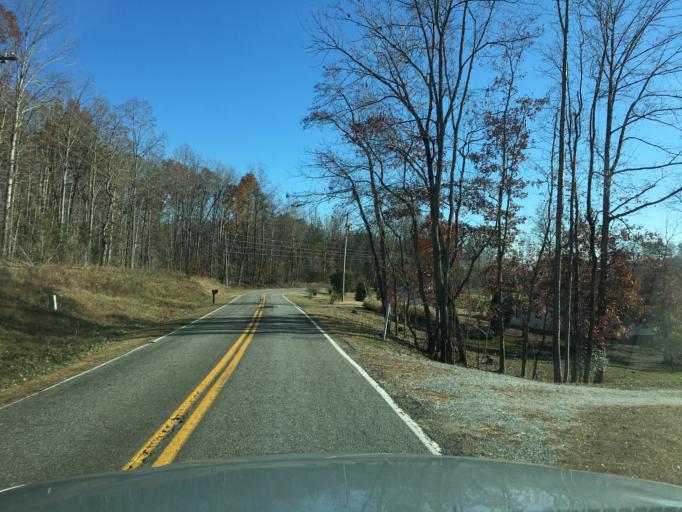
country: US
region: North Carolina
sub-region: Rutherford County
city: Rutherfordton
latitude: 35.2736
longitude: -82.0327
